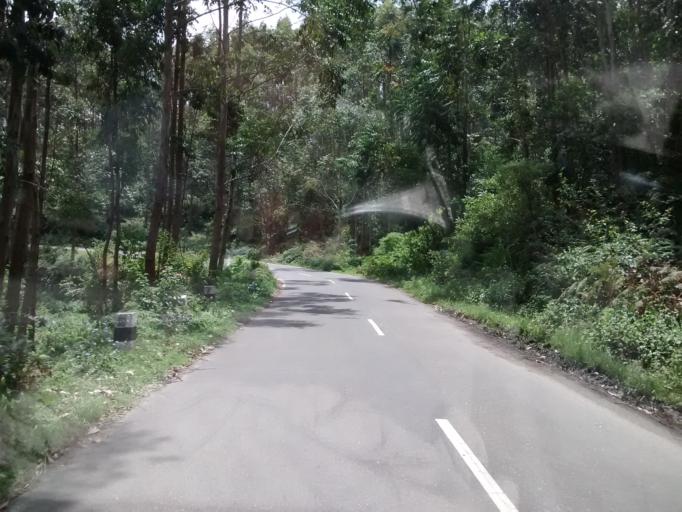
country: IN
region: Kerala
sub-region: Idukki
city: Munnar
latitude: 10.1304
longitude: 77.1695
